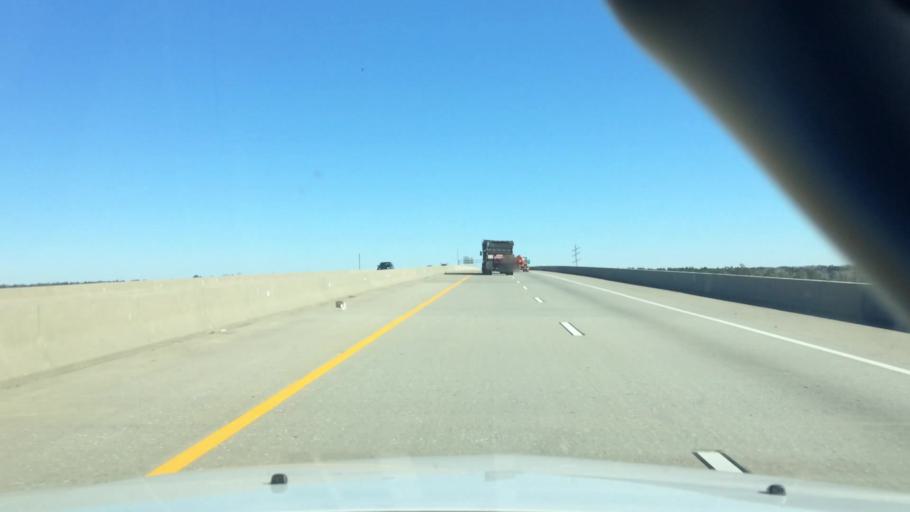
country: US
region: North Carolina
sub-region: New Hanover County
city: Wrightsboro
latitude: 34.2975
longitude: -77.9608
